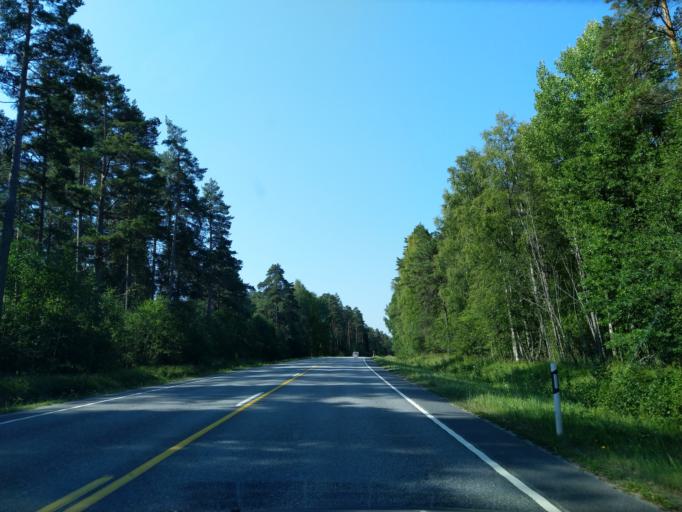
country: FI
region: Satakunta
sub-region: Pori
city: Noormarkku
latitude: 61.6011
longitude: 21.8759
